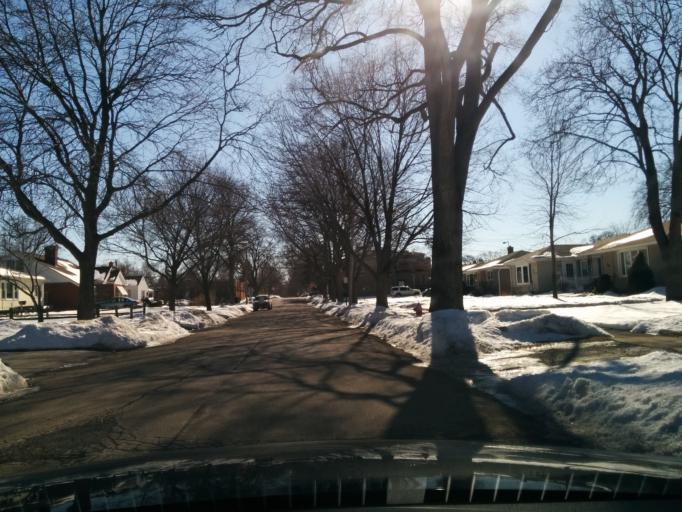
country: US
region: Illinois
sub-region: DuPage County
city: Villa Park
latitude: 41.8912
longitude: -87.9751
